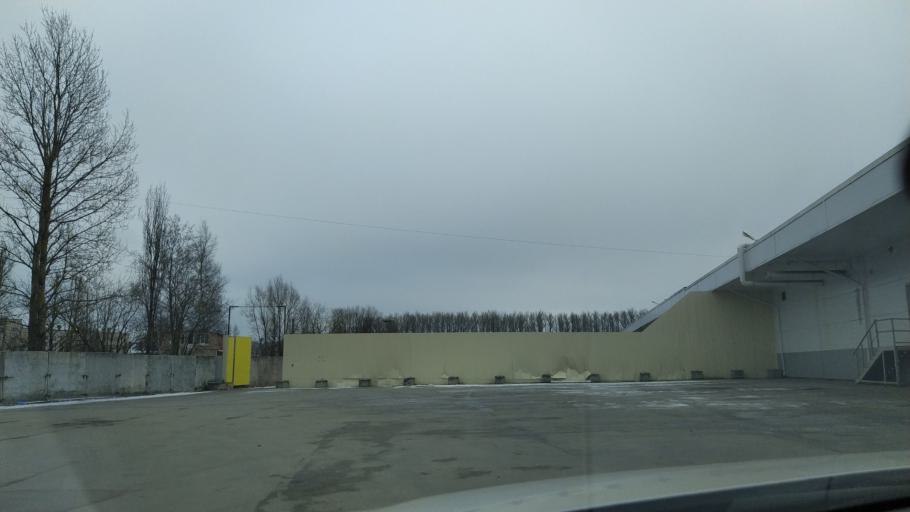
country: RU
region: St.-Petersburg
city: Pushkin
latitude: 59.7325
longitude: 30.3812
